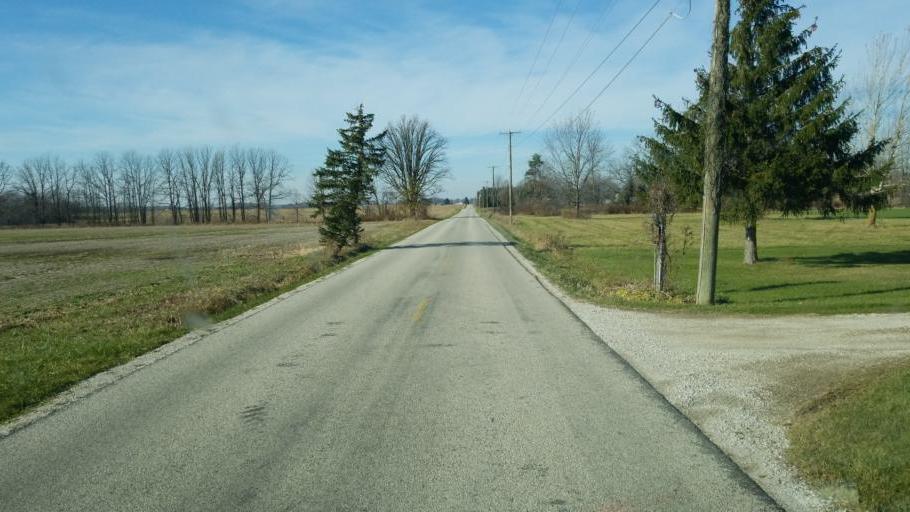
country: US
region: Ohio
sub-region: Richland County
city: Shelby
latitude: 40.8431
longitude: -82.6370
